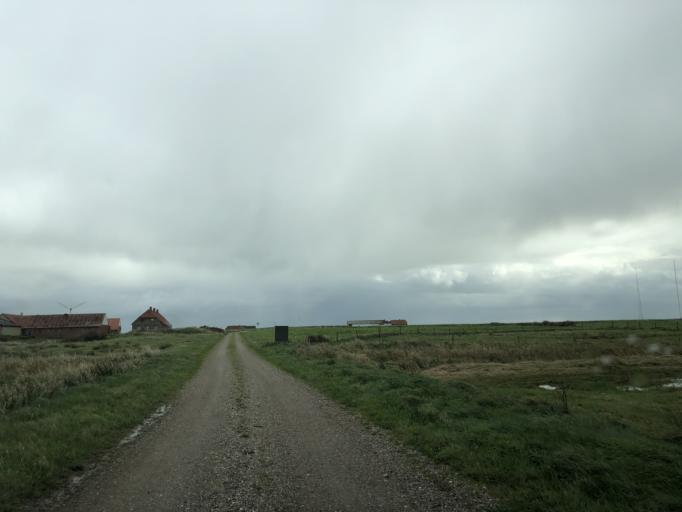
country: DK
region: Central Jutland
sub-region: Lemvig Kommune
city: Harboore
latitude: 56.4627
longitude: 8.1301
